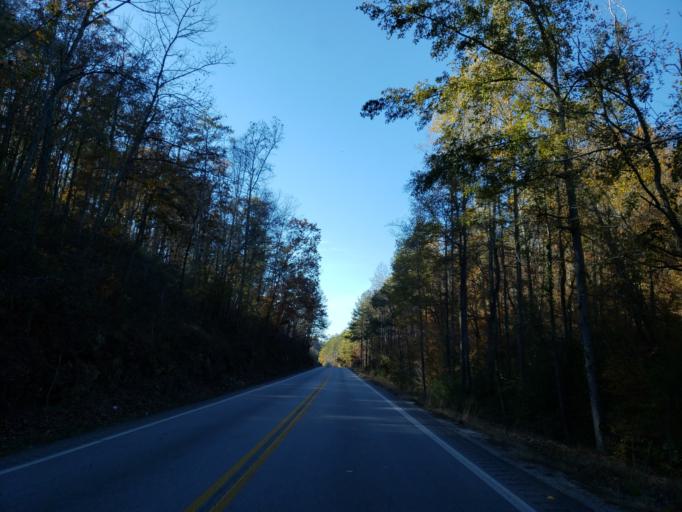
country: US
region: Alabama
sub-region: Calhoun County
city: Choccolocco
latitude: 33.5926
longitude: -85.6928
